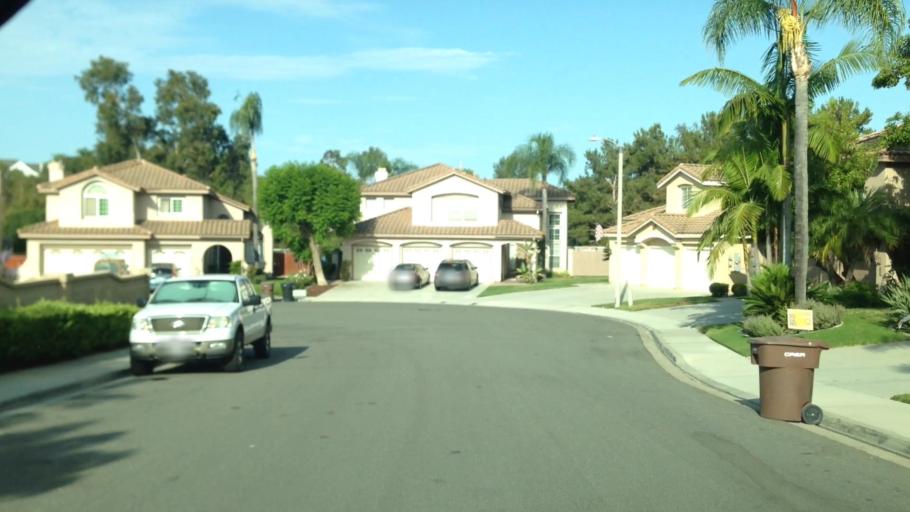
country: US
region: California
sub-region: Orange County
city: Rancho Santa Margarita
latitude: 33.6453
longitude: -117.6234
